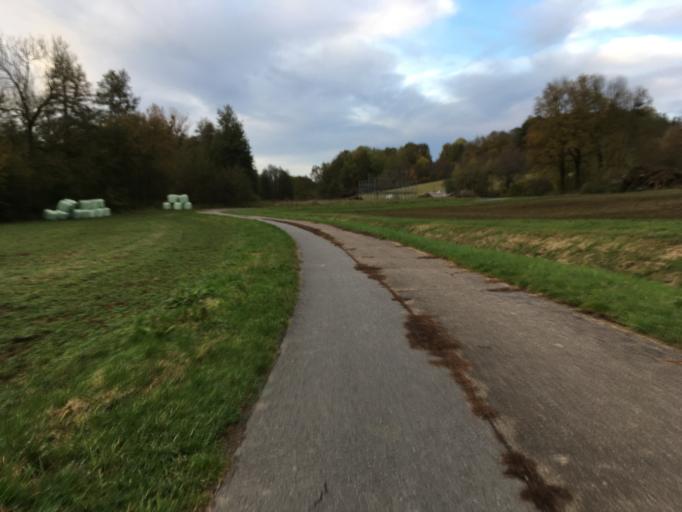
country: DE
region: Baden-Wuerttemberg
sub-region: Karlsruhe Region
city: Rosenberg
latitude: 49.3872
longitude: 9.5018
